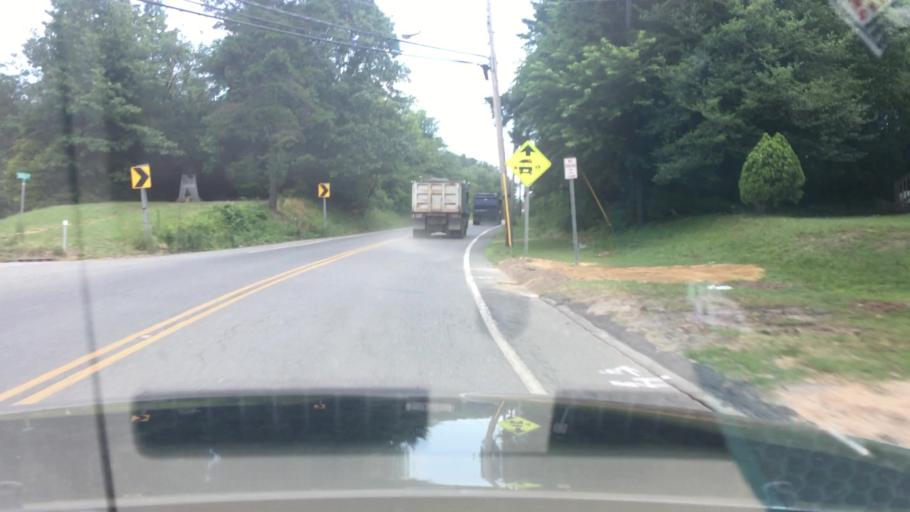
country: US
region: New Jersey
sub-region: Ocean County
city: Vista Center
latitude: 40.1118
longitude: -74.3898
